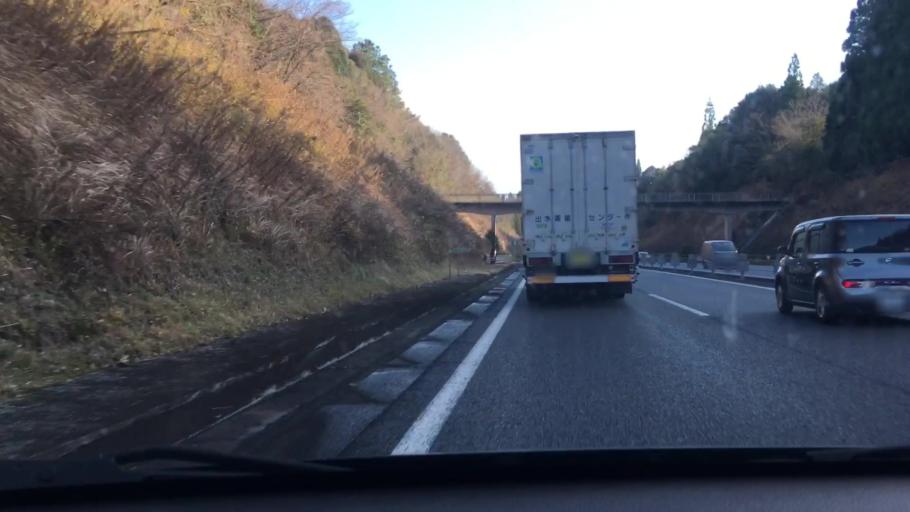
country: JP
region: Kagoshima
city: Okuchi-shinohara
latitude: 31.9113
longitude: 130.7050
